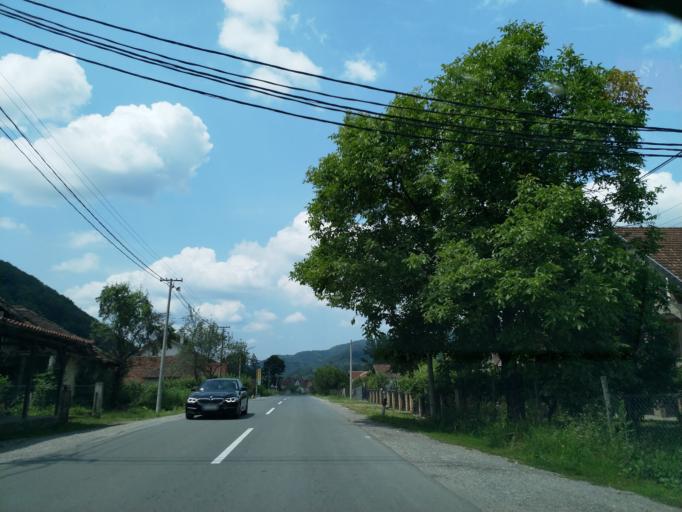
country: RS
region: Central Serbia
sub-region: Rasinski Okrug
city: Aleksandrovac
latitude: 43.3483
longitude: 21.0829
